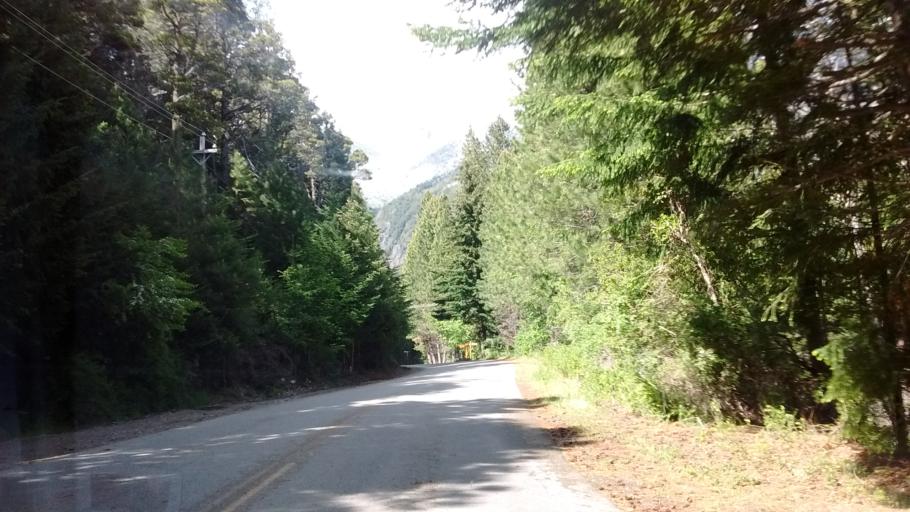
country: AR
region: Rio Negro
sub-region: Departamento de Bariloche
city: San Carlos de Bariloche
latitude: -41.0736
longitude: -71.5446
